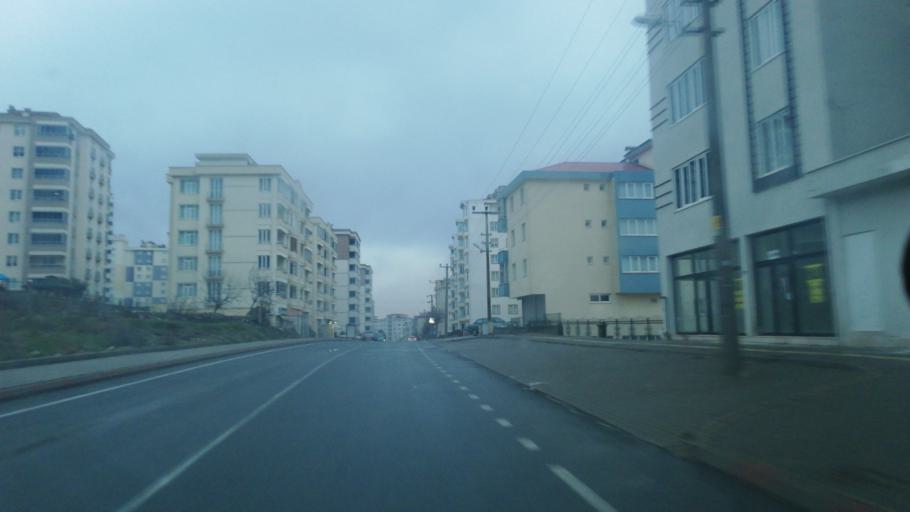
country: TR
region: Kahramanmaras
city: Kahramanmaras
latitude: 37.6003
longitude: 36.8843
